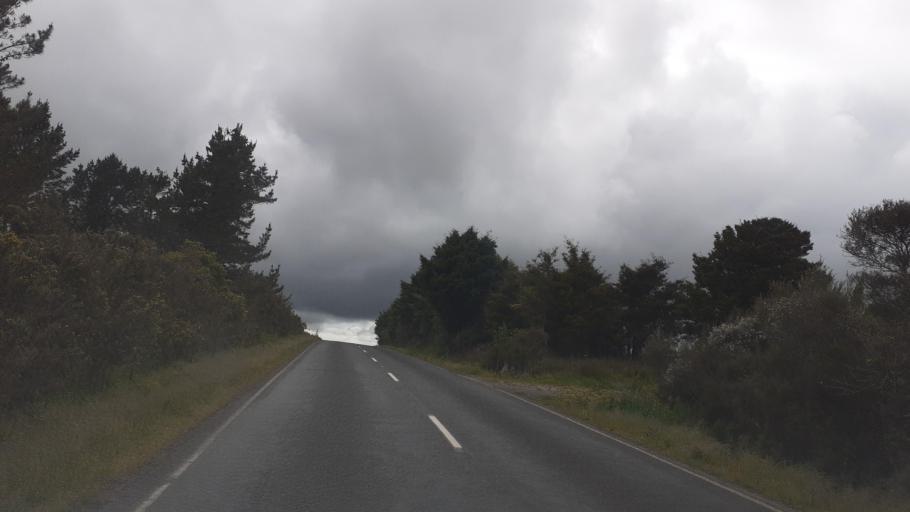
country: NZ
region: Northland
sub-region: Far North District
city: Waimate North
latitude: -35.2640
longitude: 173.8131
